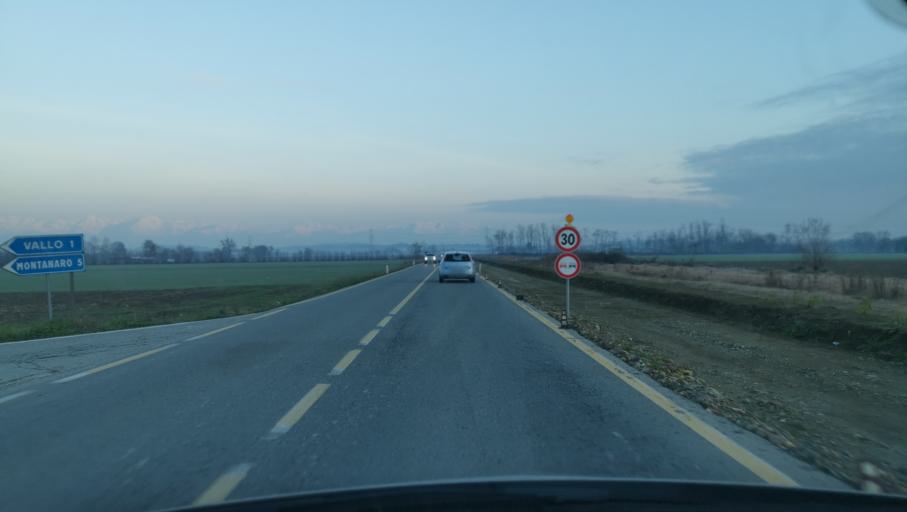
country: IT
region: Piedmont
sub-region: Provincia di Torino
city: Caluso
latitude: 45.2665
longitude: 7.8923
